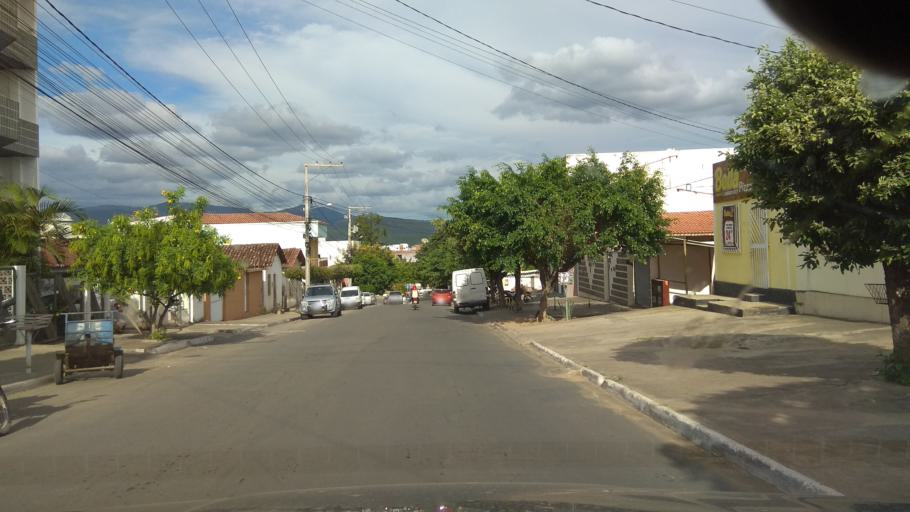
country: BR
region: Bahia
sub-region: Jequie
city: Jequie
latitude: -13.8708
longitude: -40.0709
